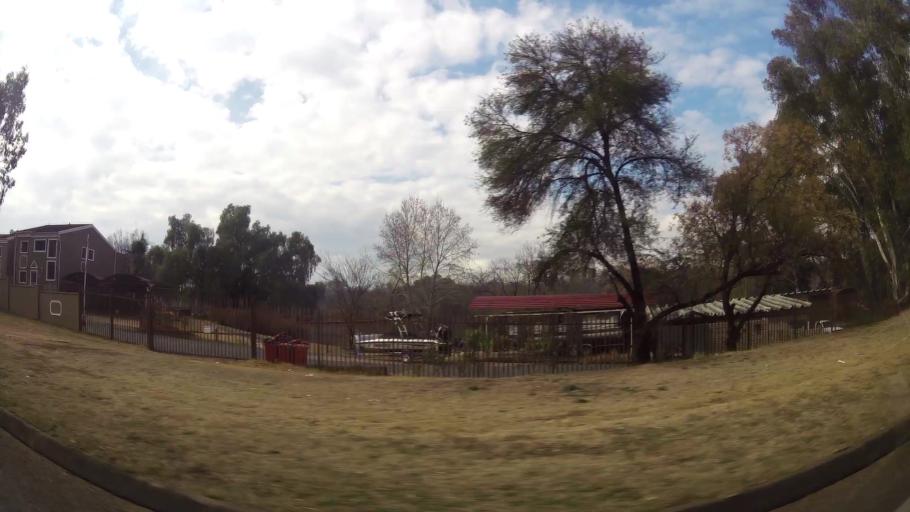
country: ZA
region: Gauteng
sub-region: Sedibeng District Municipality
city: Vereeniging
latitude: -26.6794
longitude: 27.9373
